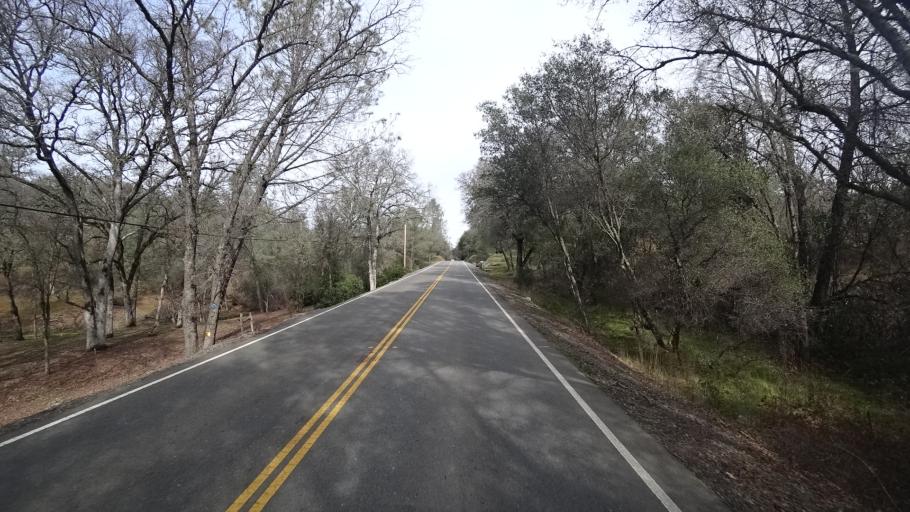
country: US
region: California
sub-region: Butte County
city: Oroville East
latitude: 39.4250
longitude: -121.4291
